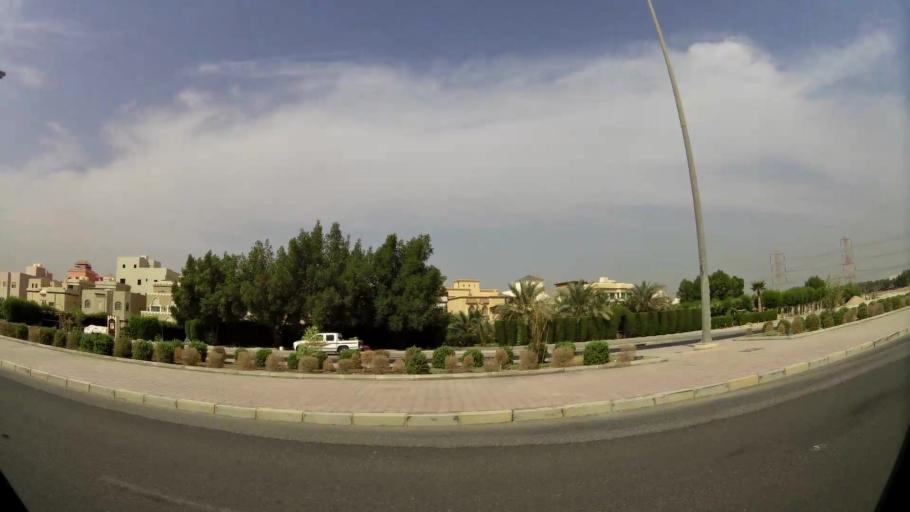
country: KW
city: Bayan
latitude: 29.2893
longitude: 48.0260
